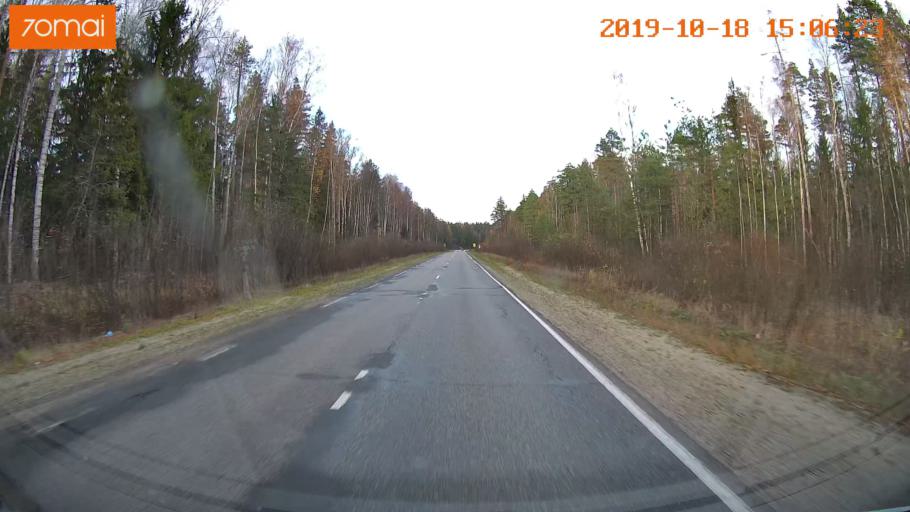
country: RU
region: Vladimir
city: Gus'-Khrustal'nyy
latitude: 55.5292
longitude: 40.5781
